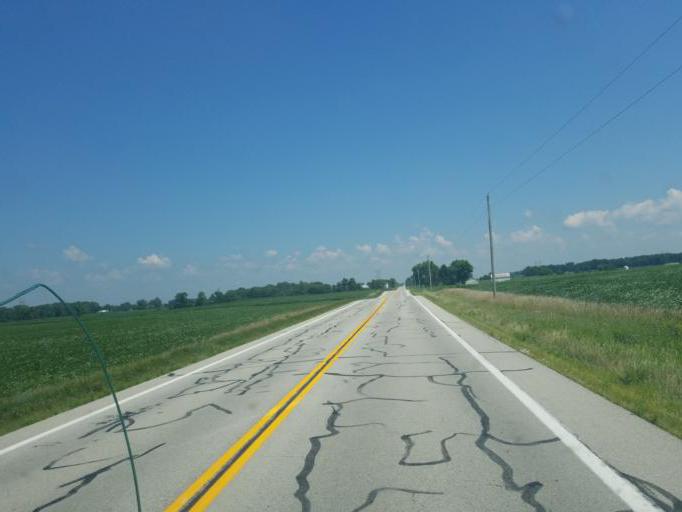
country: US
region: Ohio
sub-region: Shelby County
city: Anna
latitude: 40.3954
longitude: -84.1183
